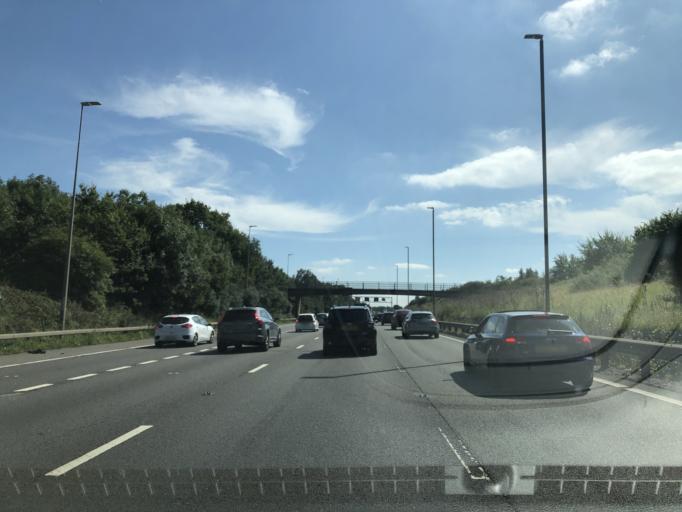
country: GB
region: England
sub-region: Solihull
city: Chelmsley Wood
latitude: 52.4903
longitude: -1.7127
